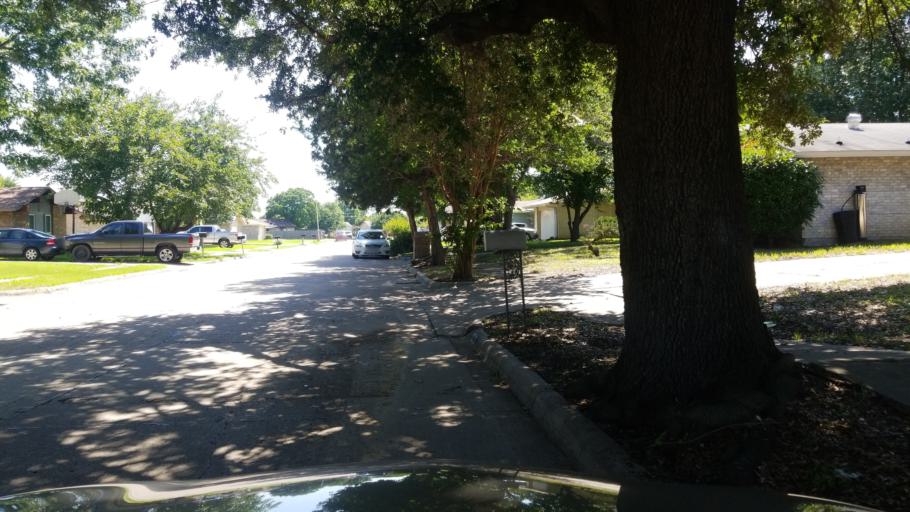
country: US
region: Texas
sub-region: Dallas County
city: Grand Prairie
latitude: 32.6874
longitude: -97.0109
